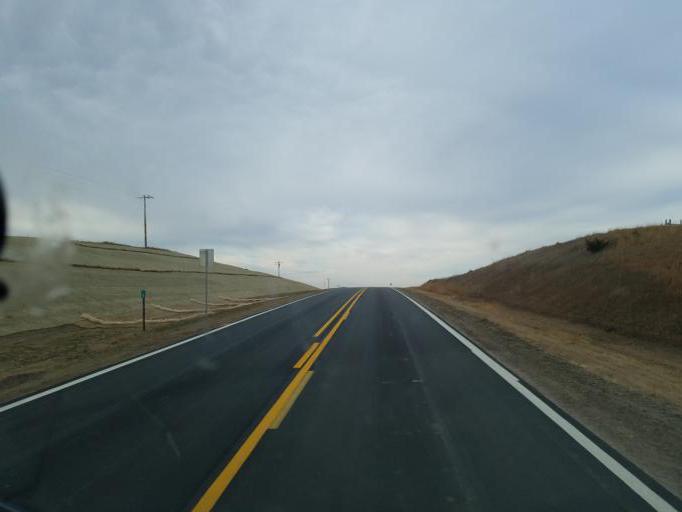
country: US
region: Nebraska
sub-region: Knox County
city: Center
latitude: 42.5971
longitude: -97.7781
